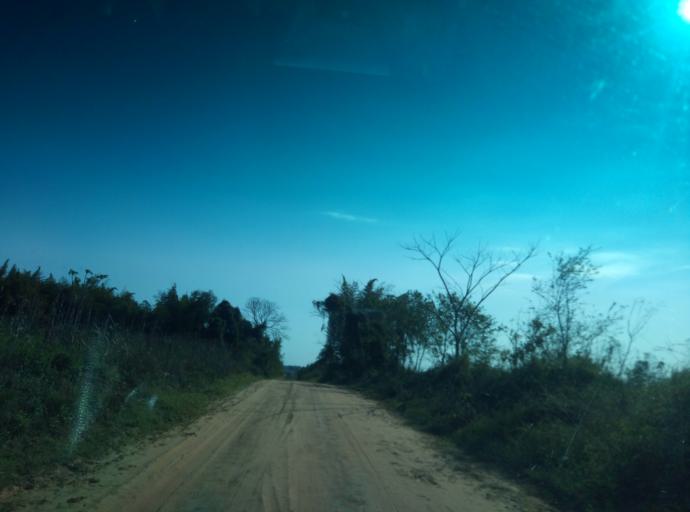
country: PY
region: Caaguazu
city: Doctor Cecilio Baez
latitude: -25.1649
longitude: -56.2152
